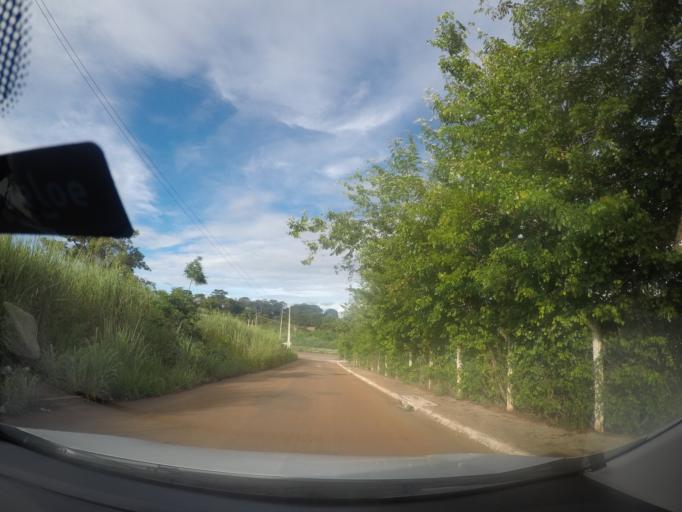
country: BR
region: Goias
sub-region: Goiania
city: Goiania
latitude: -16.6330
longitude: -49.3486
